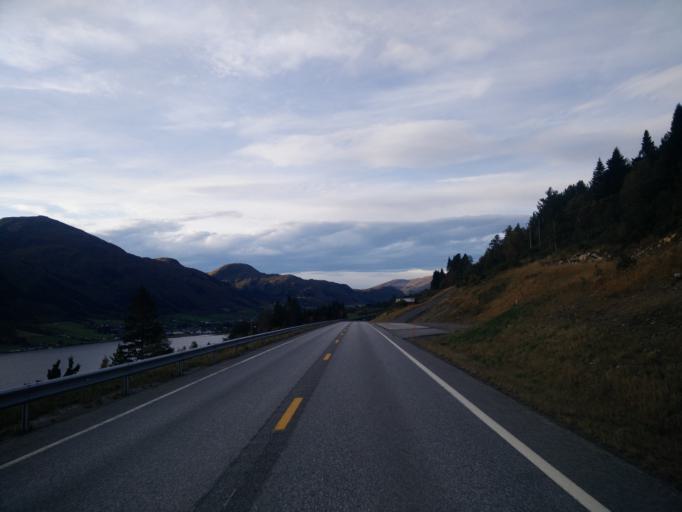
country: NO
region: More og Romsdal
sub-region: Gjemnes
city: Batnfjordsora
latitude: 62.9137
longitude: 7.6894
